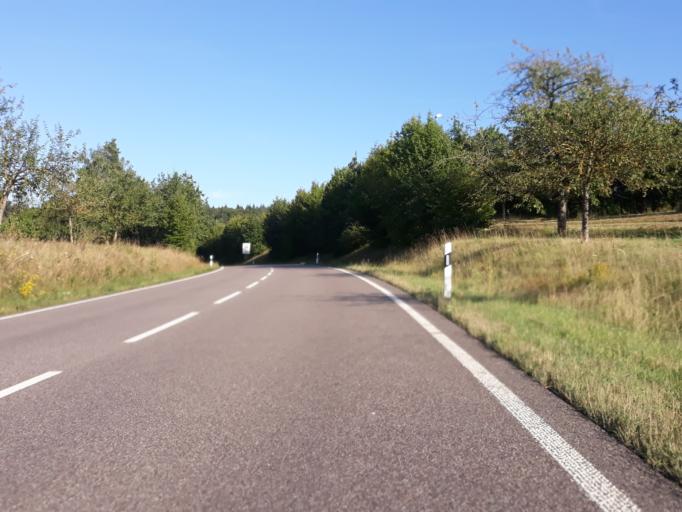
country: DE
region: Baden-Wuerttemberg
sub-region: Regierungsbezirk Stuttgart
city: Nufringen
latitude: 48.6145
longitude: 8.8776
